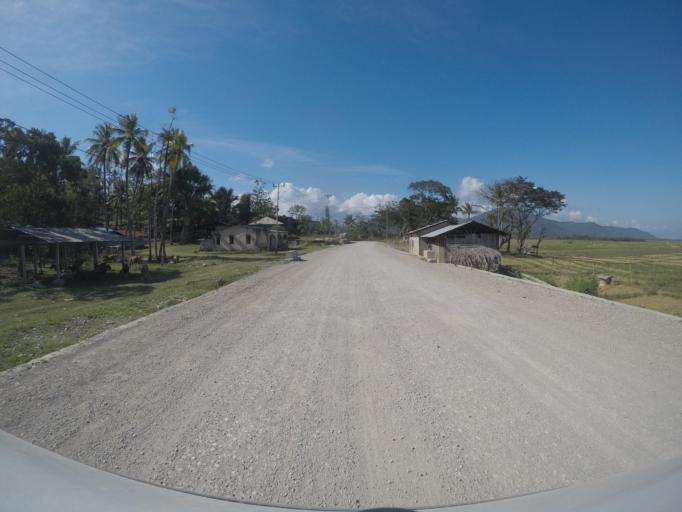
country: TL
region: Viqueque
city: Viqueque
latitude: -8.8198
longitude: 126.5329
